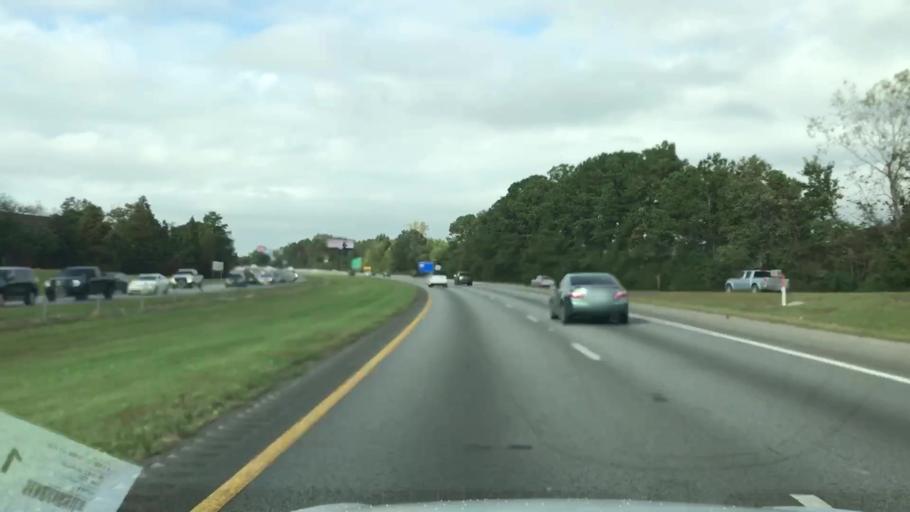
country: US
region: South Carolina
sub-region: Charleston County
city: North Charleston
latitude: 32.8429
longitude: -80.0182
